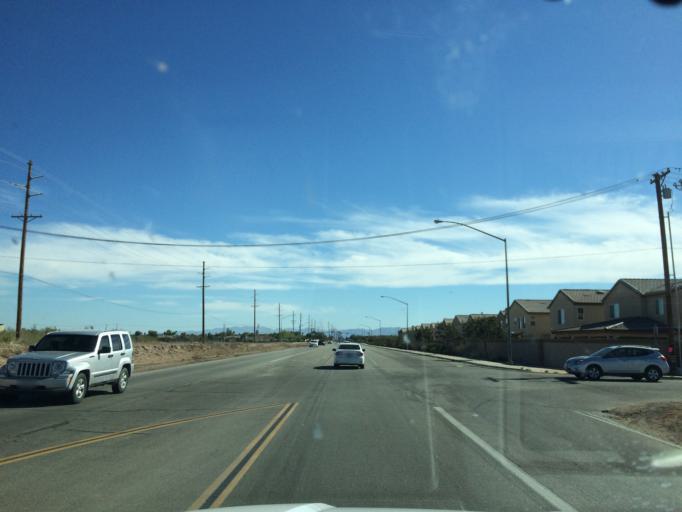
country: US
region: California
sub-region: Imperial County
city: Heber
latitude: 32.7419
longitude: -115.5347
